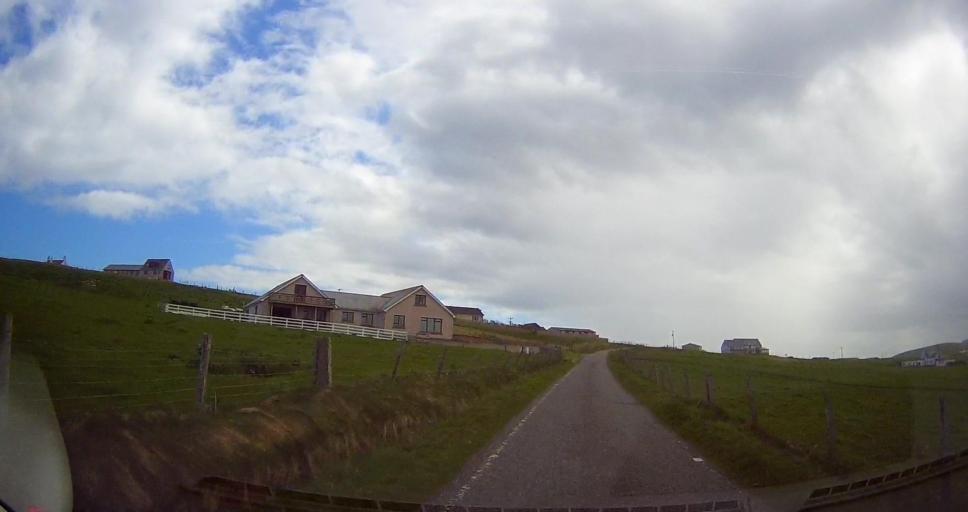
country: GB
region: Scotland
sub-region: Shetland Islands
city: Sandwick
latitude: 59.9186
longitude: -1.3203
